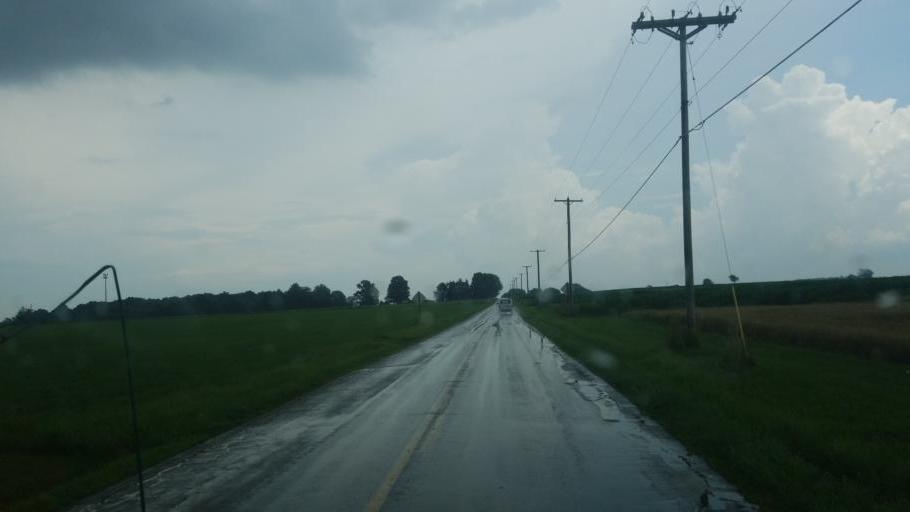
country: US
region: Ohio
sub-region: Wayne County
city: Orrville
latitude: 40.9019
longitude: -81.8013
